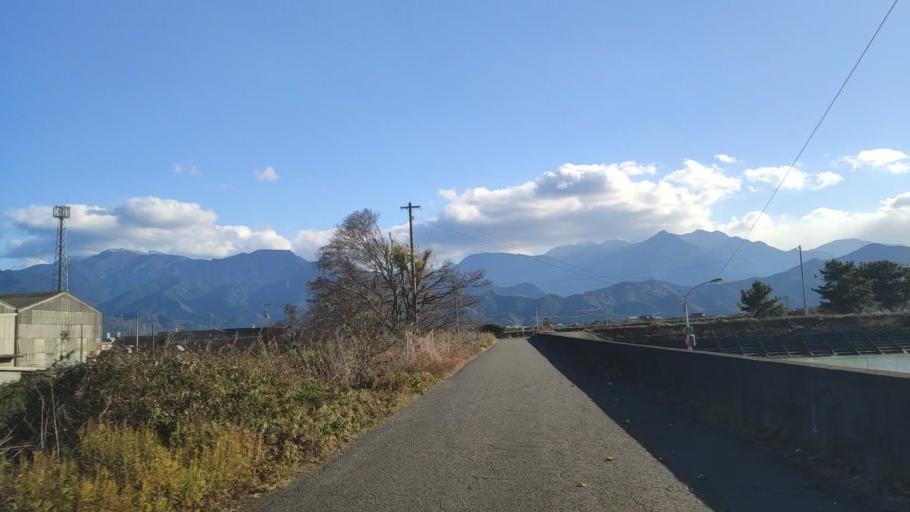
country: JP
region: Ehime
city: Saijo
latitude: 33.9215
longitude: 133.1561
